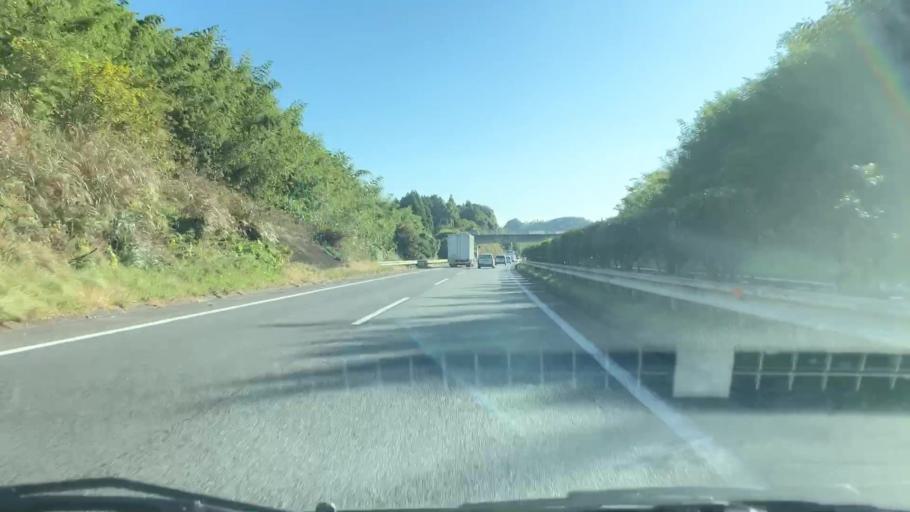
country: JP
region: Saga Prefecture
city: Saga-shi
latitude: 33.3111
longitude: 130.2143
